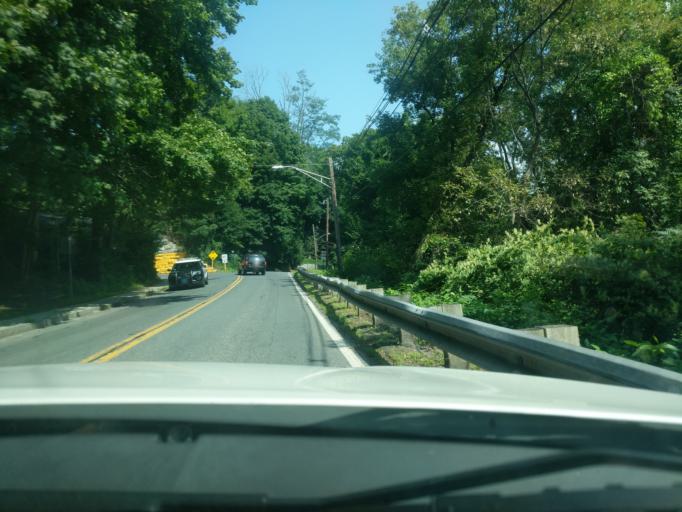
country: US
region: Massachusetts
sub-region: Berkshire County
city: Great Barrington
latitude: 42.2028
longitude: -73.3583
